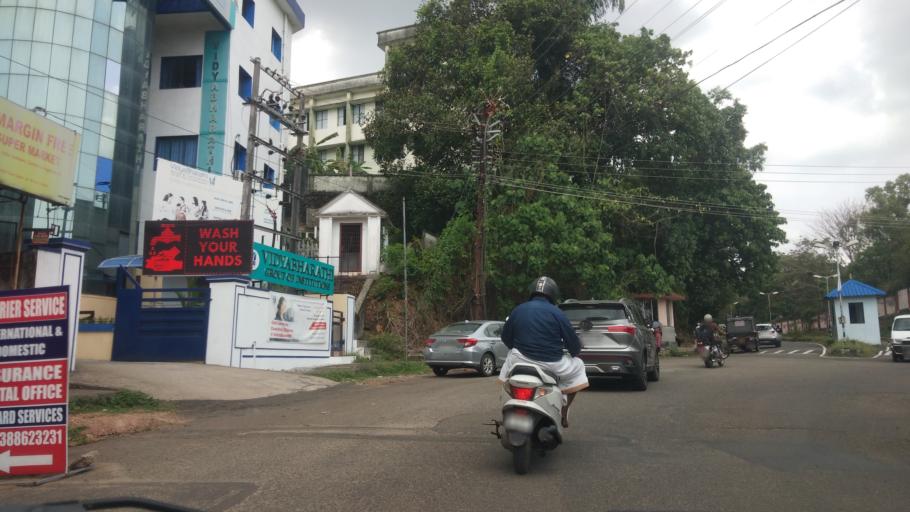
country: IN
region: Kerala
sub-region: Ernakulam
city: Elur
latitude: 10.0460
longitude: 76.3232
